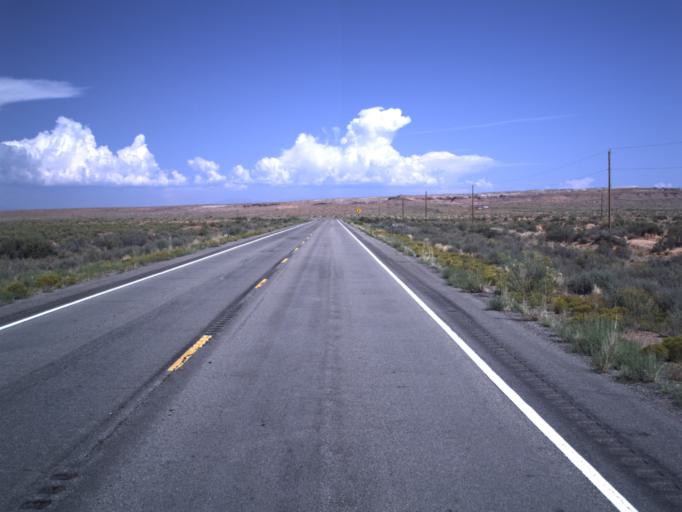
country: US
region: Utah
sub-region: San Juan County
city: Blanding
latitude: 37.1158
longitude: -109.5453
